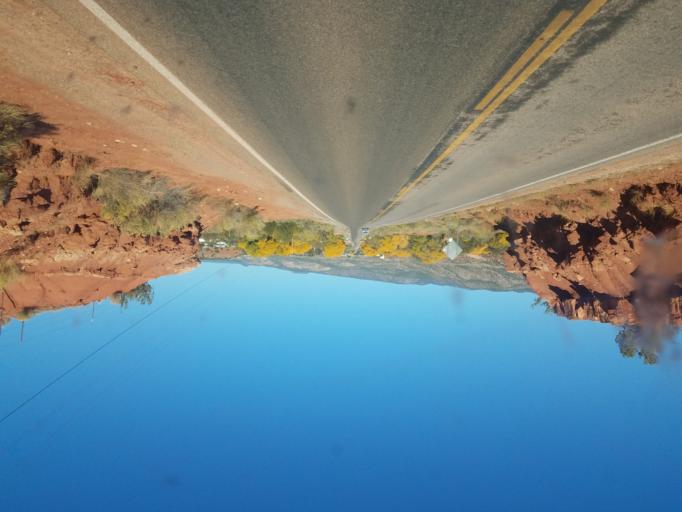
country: US
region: New Mexico
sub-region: Sandoval County
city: Jemez Pueblo
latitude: 35.6480
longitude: -106.7283
